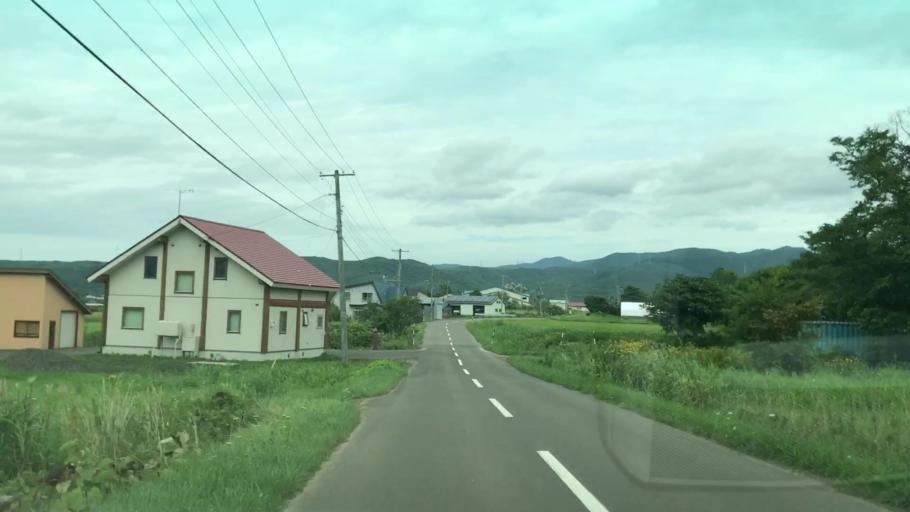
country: JP
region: Hokkaido
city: Iwanai
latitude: 43.0267
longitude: 140.5684
